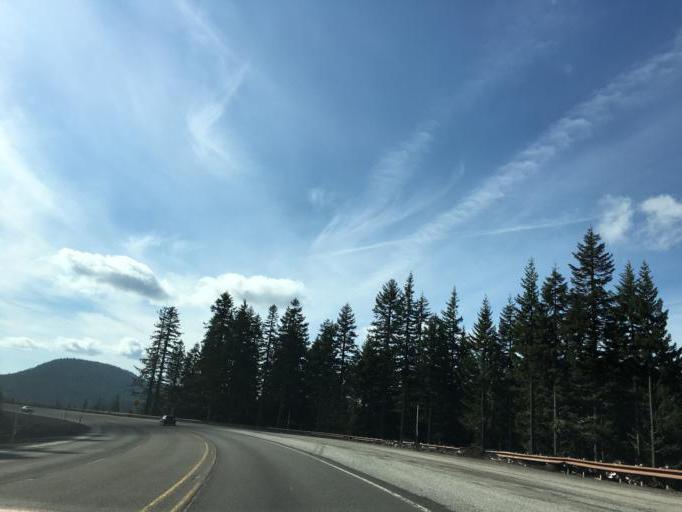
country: US
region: Oregon
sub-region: Clackamas County
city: Mount Hood Village
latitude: 45.2916
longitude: -121.7353
